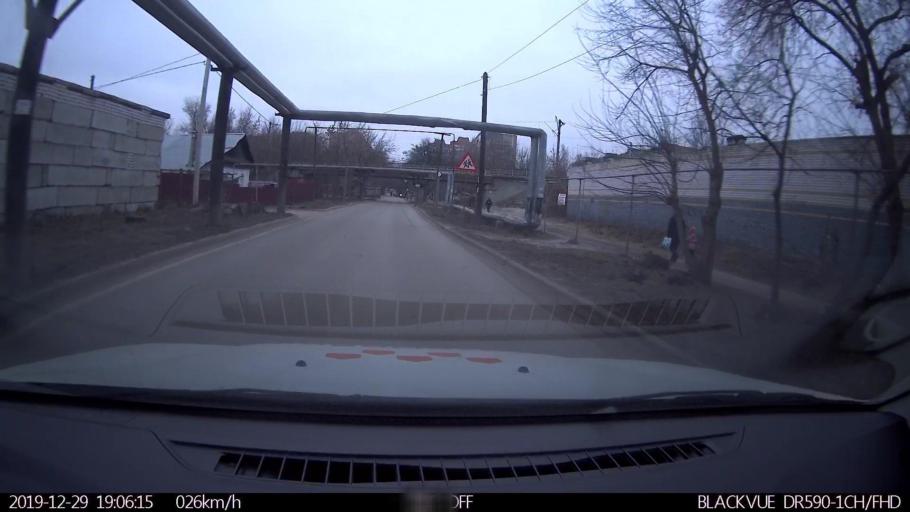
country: RU
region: Nizjnij Novgorod
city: Neklyudovo
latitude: 56.3569
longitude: 43.8611
